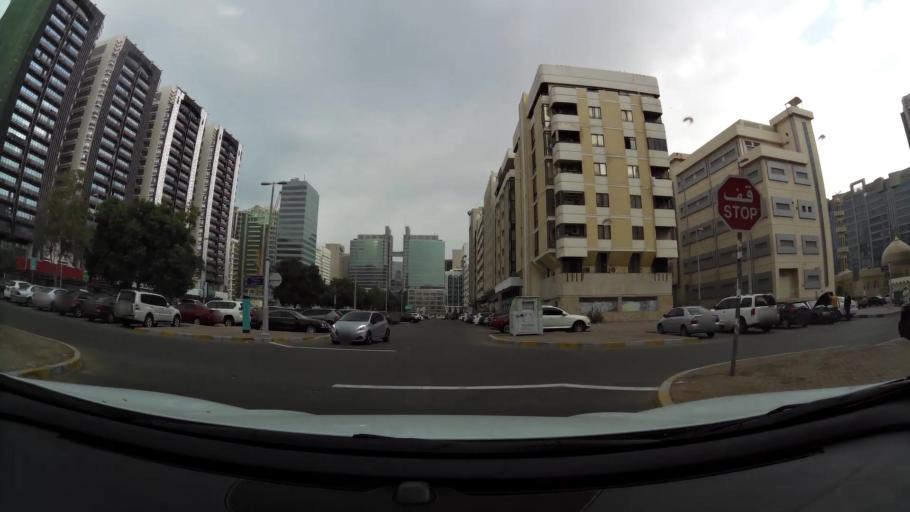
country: AE
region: Abu Dhabi
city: Abu Dhabi
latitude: 24.4921
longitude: 54.3789
